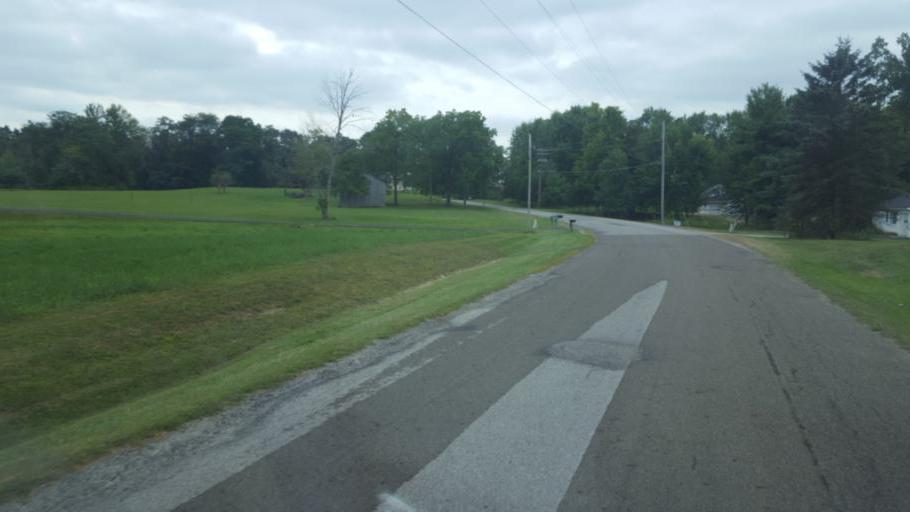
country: US
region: Ohio
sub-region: Morrow County
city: Mount Gilead
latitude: 40.5662
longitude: -82.8438
